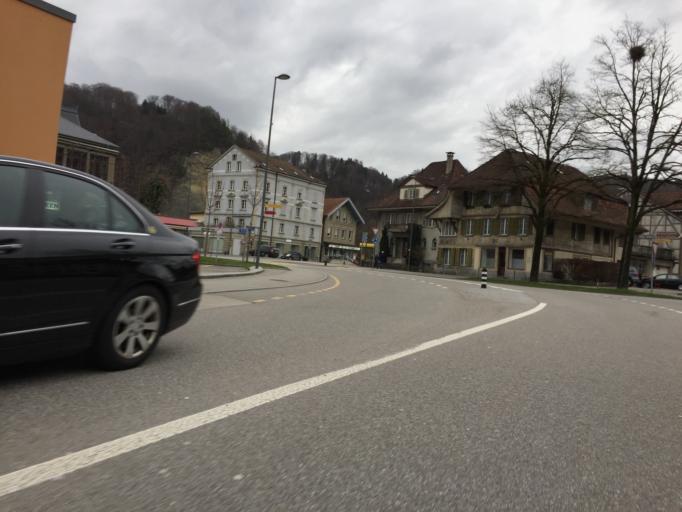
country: CH
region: Bern
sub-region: Emmental District
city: Burgdorf
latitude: 47.0581
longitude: 7.6277
